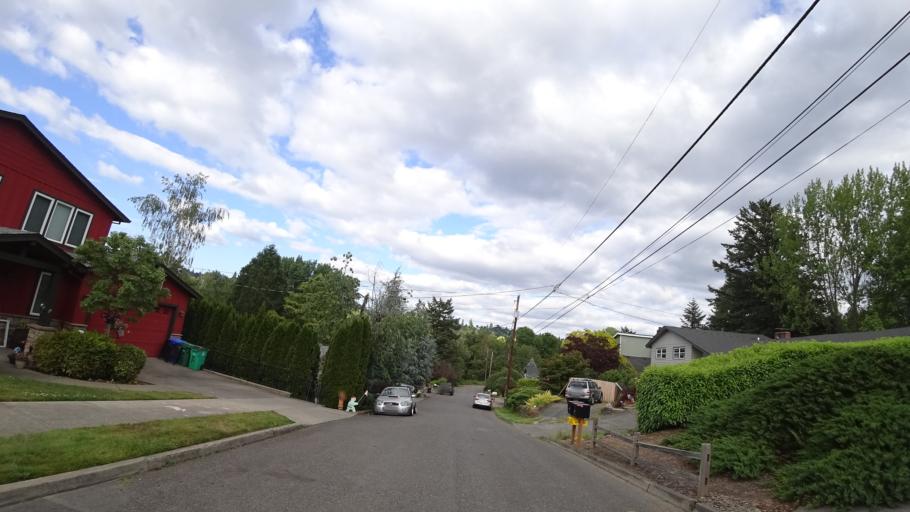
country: US
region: Oregon
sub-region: Washington County
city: Garden Home-Whitford
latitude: 45.4741
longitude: -122.7288
